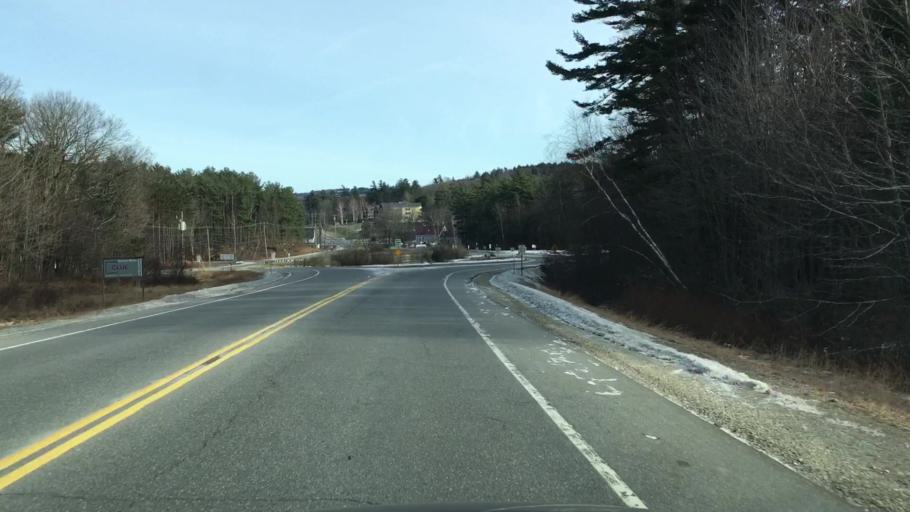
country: US
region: New Hampshire
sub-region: Merrimack County
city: Newbury
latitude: 43.3410
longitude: -72.0738
